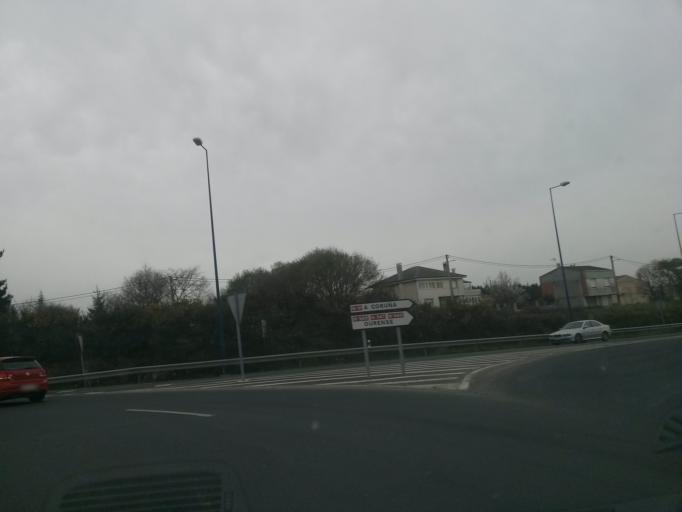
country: ES
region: Galicia
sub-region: Provincia de Lugo
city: Lugo
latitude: 43.0344
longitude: -7.5555
